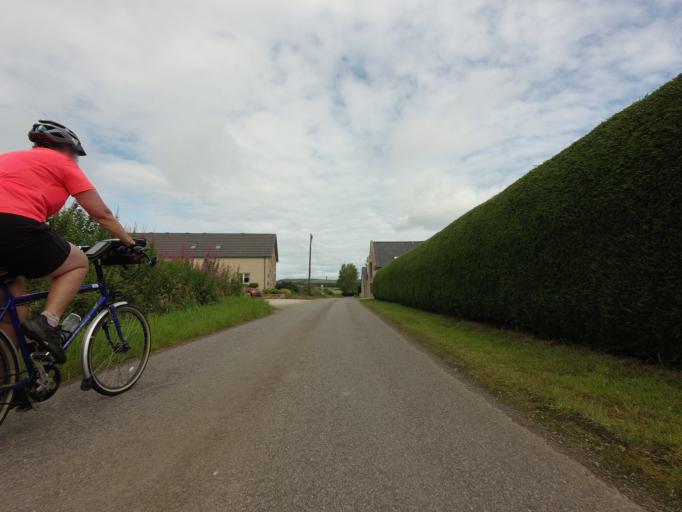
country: GB
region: Scotland
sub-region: Moray
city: Elgin
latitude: 57.6629
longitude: -3.3697
